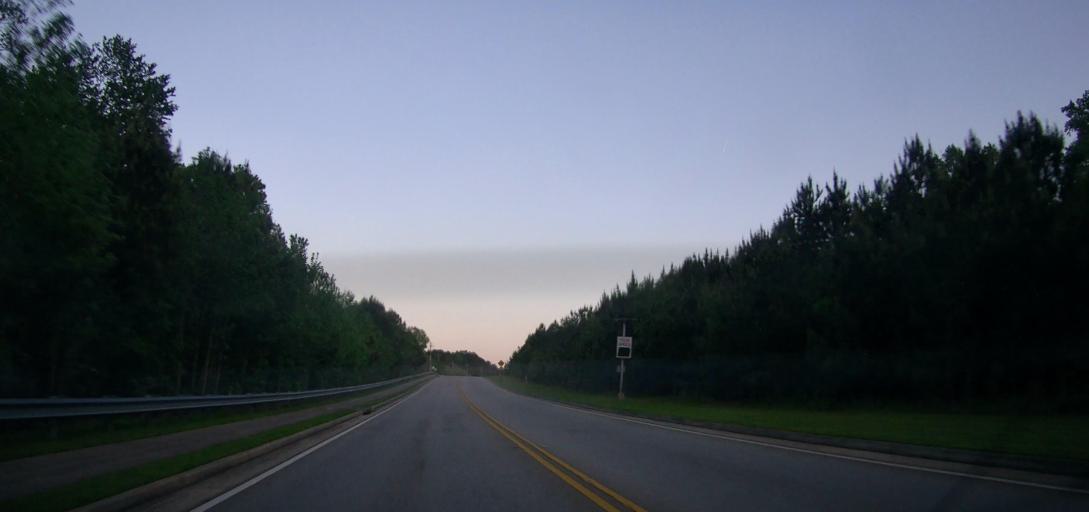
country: US
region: Georgia
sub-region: Henry County
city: Stockbridge
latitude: 33.5012
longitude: -84.2231
